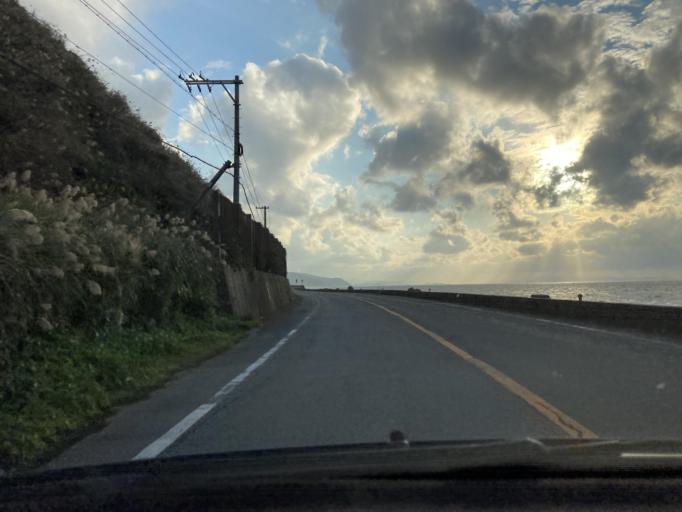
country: JP
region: Okinawa
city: Nago
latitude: 26.8140
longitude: 128.2359
